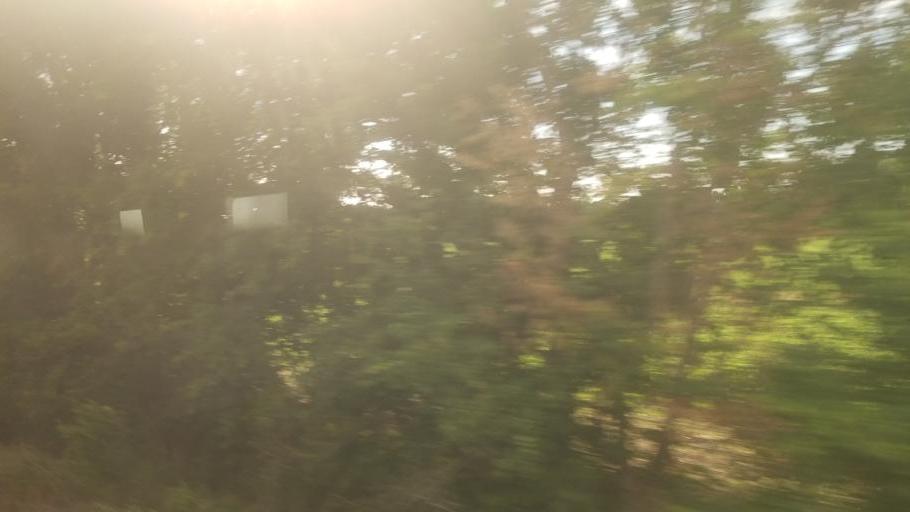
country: US
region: Kansas
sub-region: Douglas County
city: Eudora
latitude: 38.9638
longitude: -95.0629
